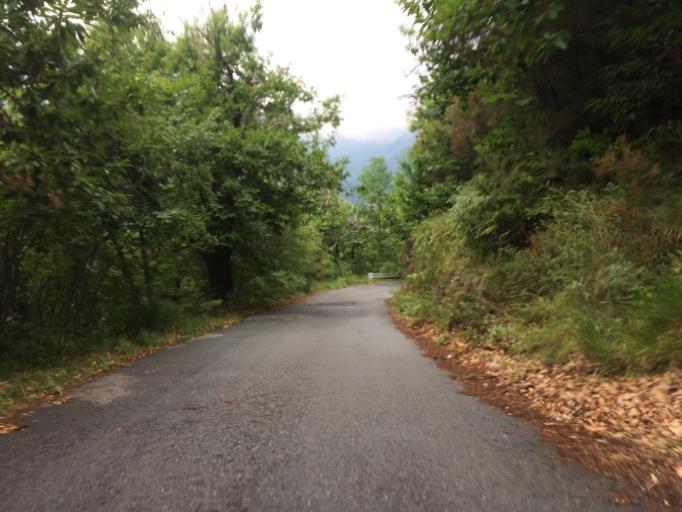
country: IT
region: Liguria
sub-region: Provincia di Imperia
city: Castel Vittorio
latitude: 43.9452
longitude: 7.6895
